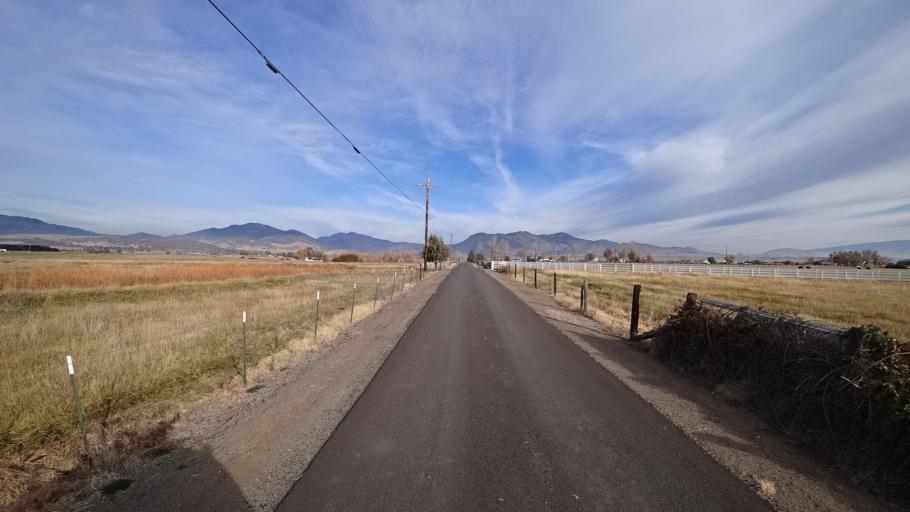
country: US
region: California
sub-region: Siskiyou County
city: Montague
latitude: 41.7280
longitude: -122.5786
